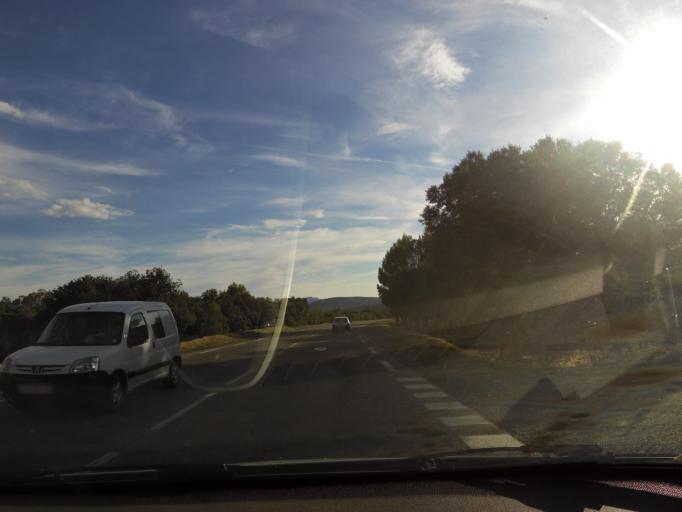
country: FR
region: Languedoc-Roussillon
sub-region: Departement du Gard
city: Quissac
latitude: 43.8753
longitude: 3.9596
